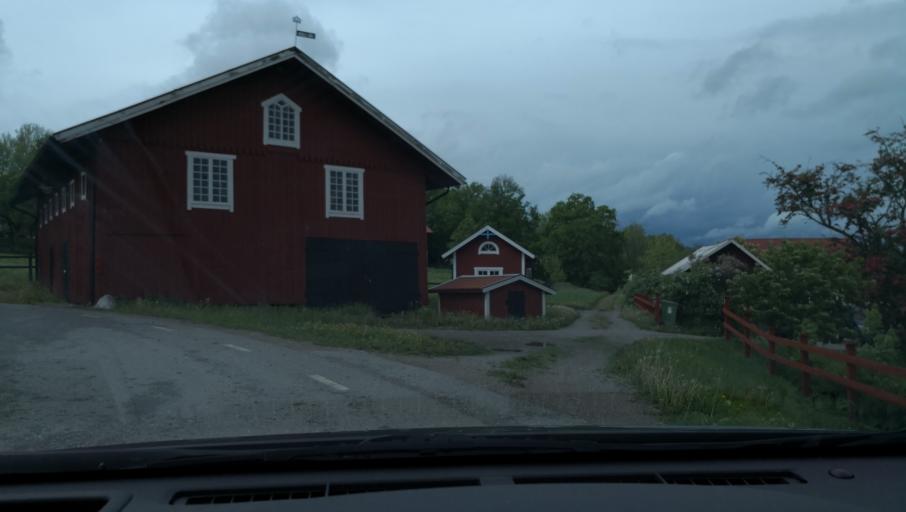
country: SE
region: Uppsala
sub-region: Enkopings Kommun
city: Orsundsbro
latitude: 59.7246
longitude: 17.4178
